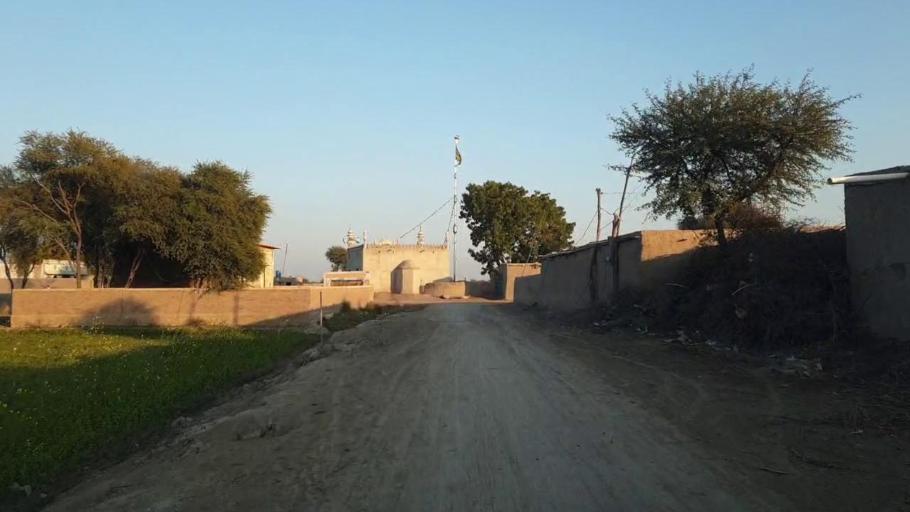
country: PK
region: Sindh
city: Shahpur Chakar
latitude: 26.1527
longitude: 68.5683
